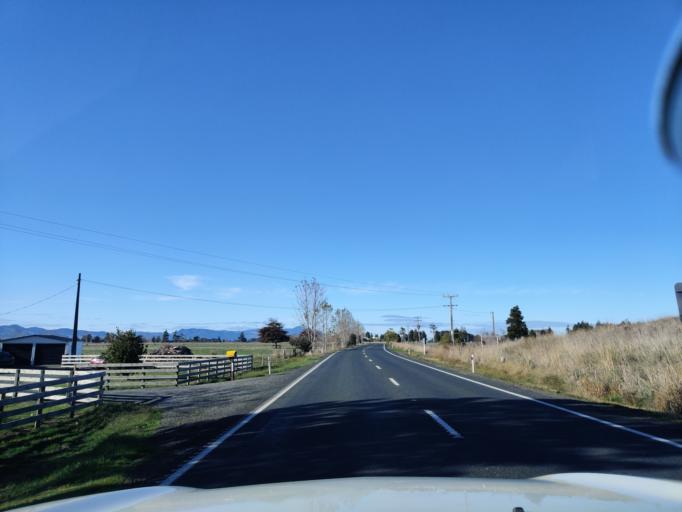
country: NZ
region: Waikato
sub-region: Hauraki District
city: Ngatea
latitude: -37.2991
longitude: 175.5574
